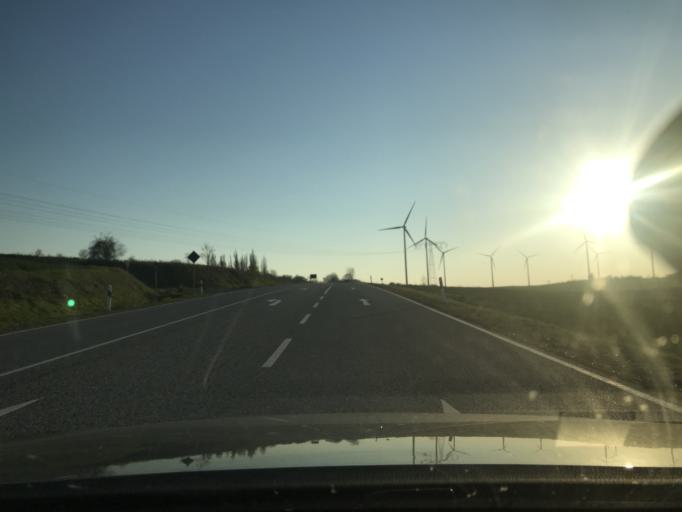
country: DE
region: Thuringia
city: Wipperdorf
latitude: 51.4678
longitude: 10.6913
